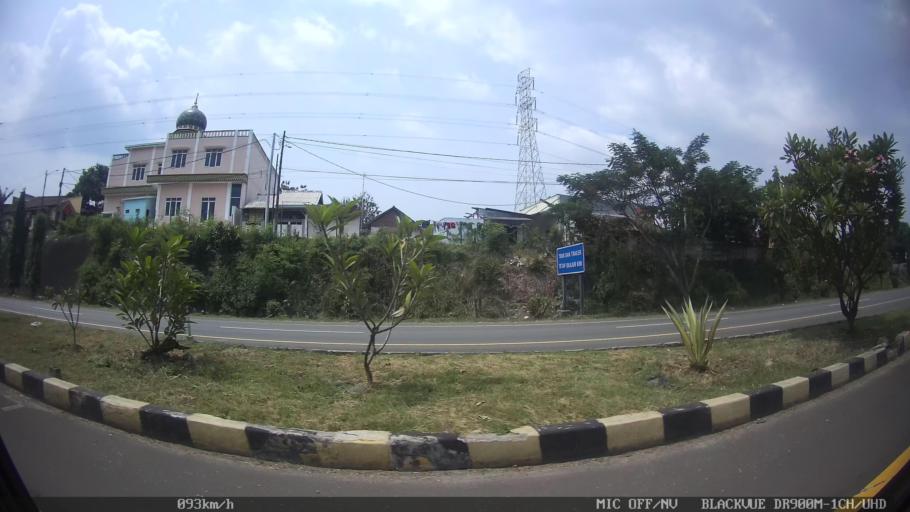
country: ID
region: Banten
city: Curug
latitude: -5.9888
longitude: 106.0393
